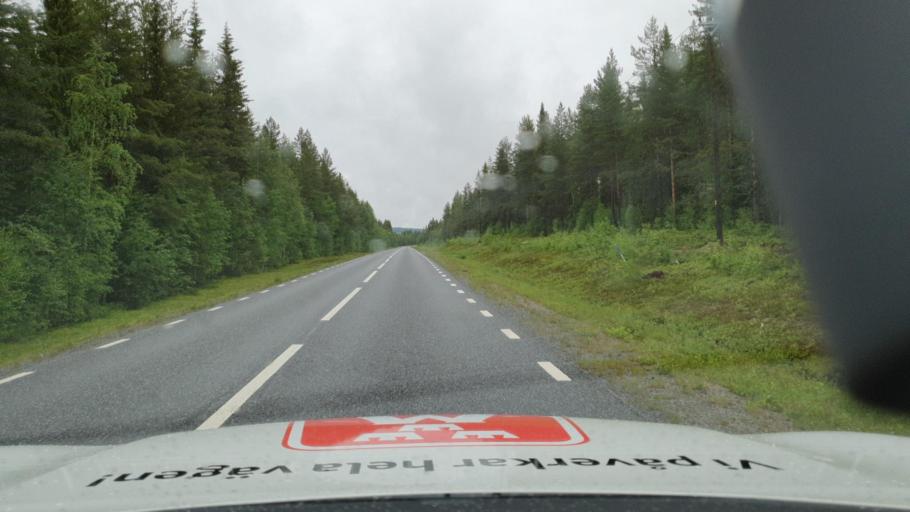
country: SE
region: Vaesterbotten
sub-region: Asele Kommun
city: Asele
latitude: 63.9874
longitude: 17.2648
